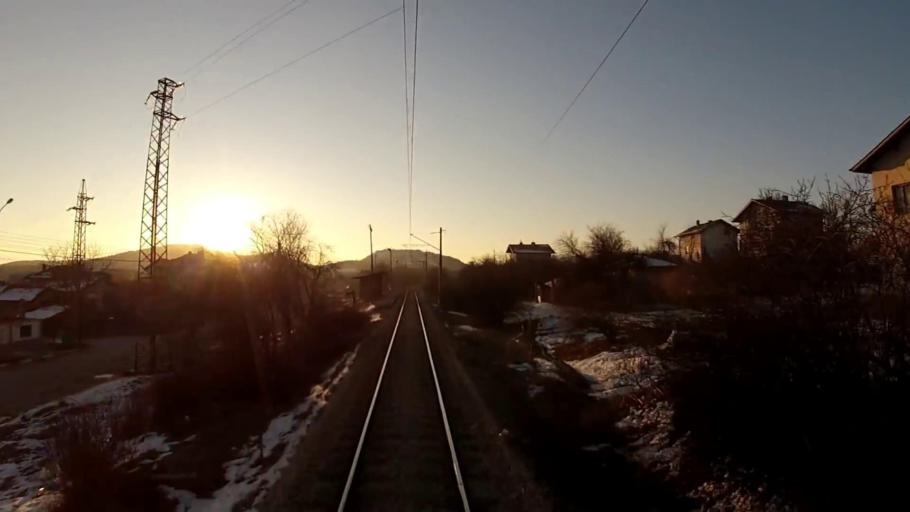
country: BG
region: Sofiya
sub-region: Obshtina Dragoman
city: Dragoman
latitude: 42.9093
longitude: 22.9436
